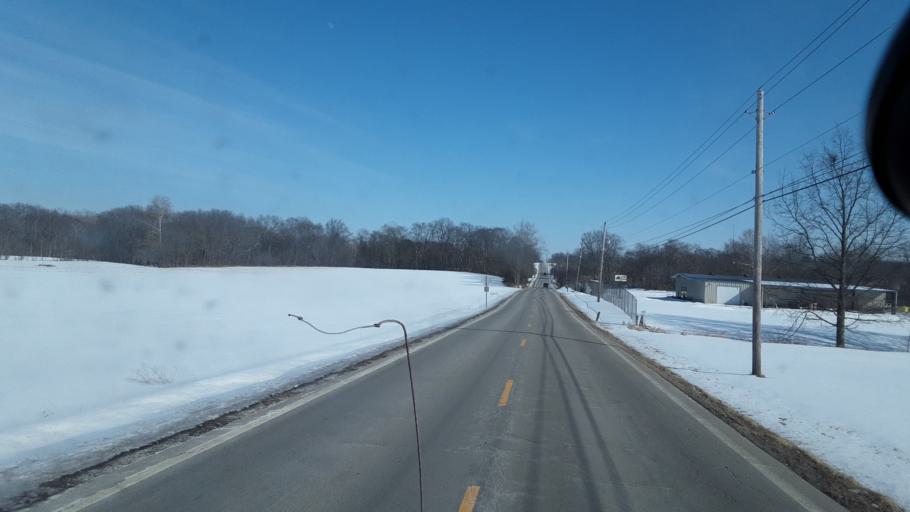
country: US
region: Ohio
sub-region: Columbiana County
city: Salem
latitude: 40.9446
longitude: -80.8838
